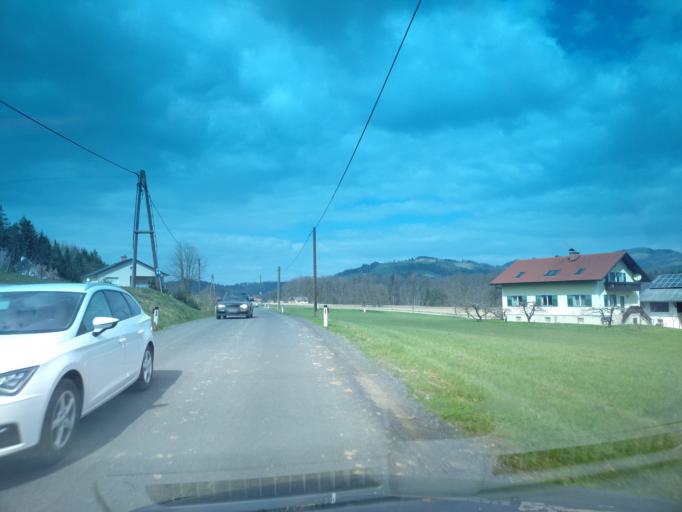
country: AT
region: Styria
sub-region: Politischer Bezirk Leibnitz
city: Grossklein
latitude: 46.7432
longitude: 15.4292
